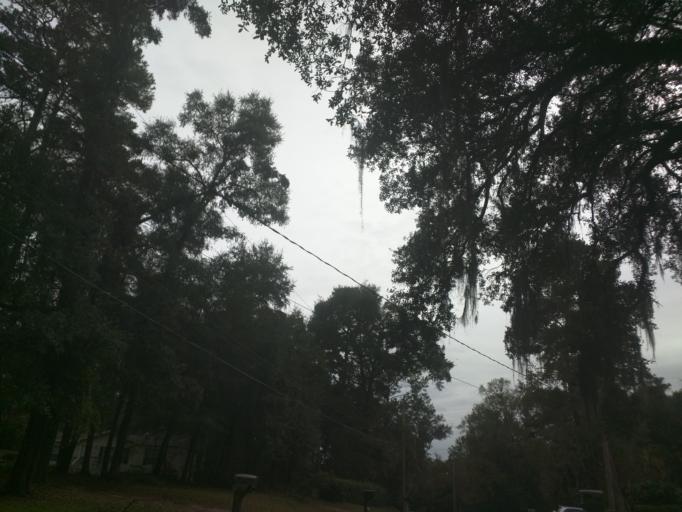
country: US
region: Florida
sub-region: Leon County
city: Tallahassee
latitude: 30.4612
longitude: -84.2346
